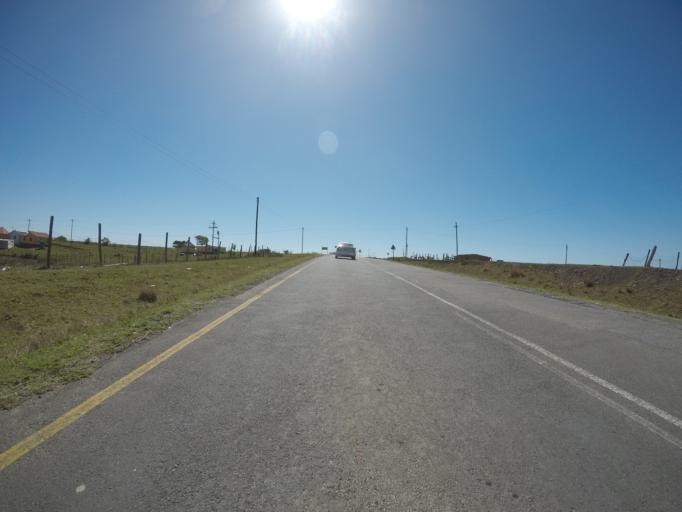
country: ZA
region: Eastern Cape
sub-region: OR Tambo District Municipality
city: Libode
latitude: -31.9209
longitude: 28.9703
